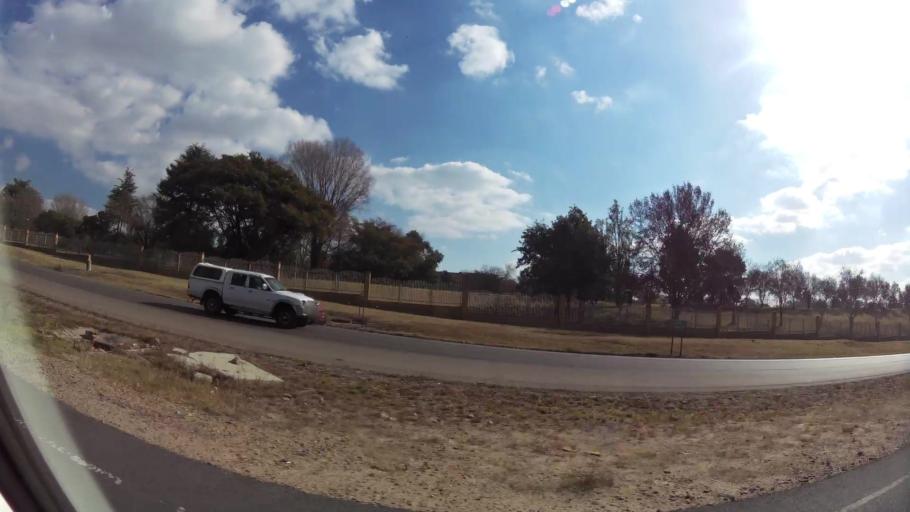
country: ZA
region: Gauteng
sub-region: City of Johannesburg Metropolitan Municipality
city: Midrand
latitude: -26.0385
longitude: 28.0910
